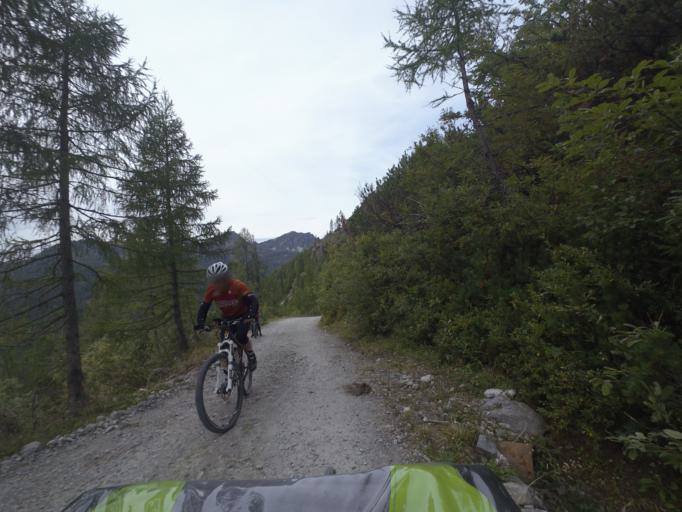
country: AT
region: Salzburg
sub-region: Politischer Bezirk Sankt Johann im Pongau
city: Untertauern
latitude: 47.2917
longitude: 13.5896
